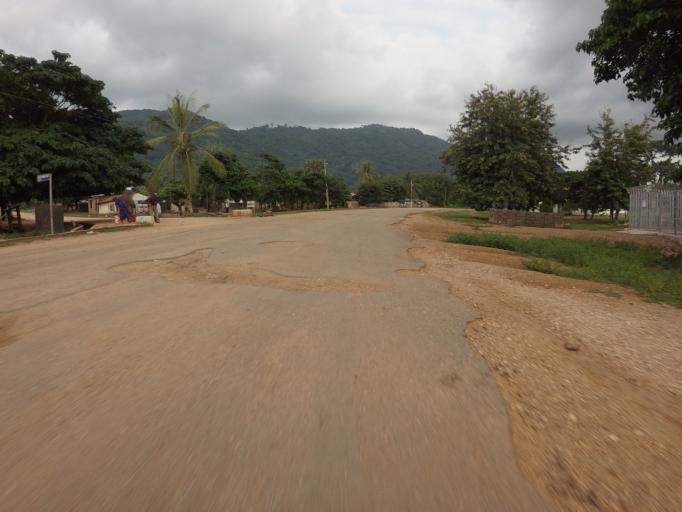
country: GH
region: Volta
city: Kpandu
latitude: 6.8138
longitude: 0.3745
